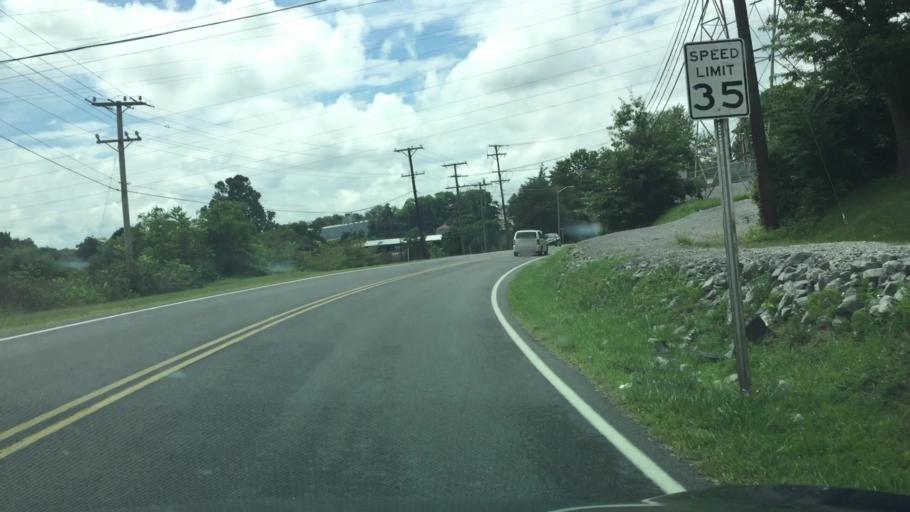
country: US
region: Virginia
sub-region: Wythe County
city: Wytheville
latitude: 36.9464
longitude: -81.0595
